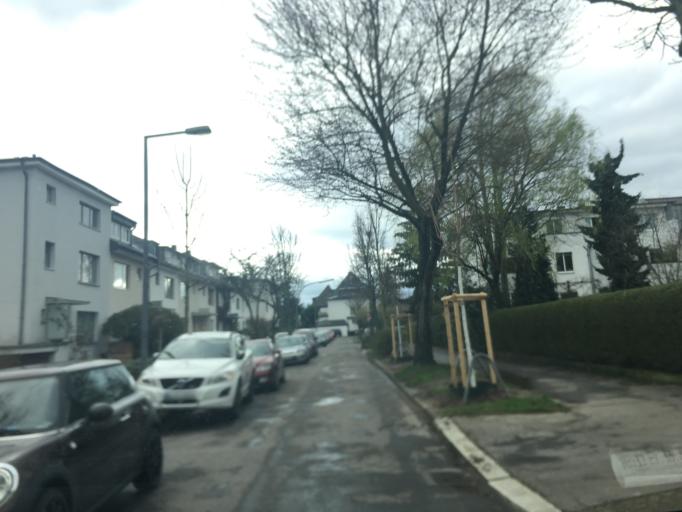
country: DE
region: North Rhine-Westphalia
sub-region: Regierungsbezirk Koln
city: Bilderstoeckchen
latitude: 50.9619
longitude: 6.9213
